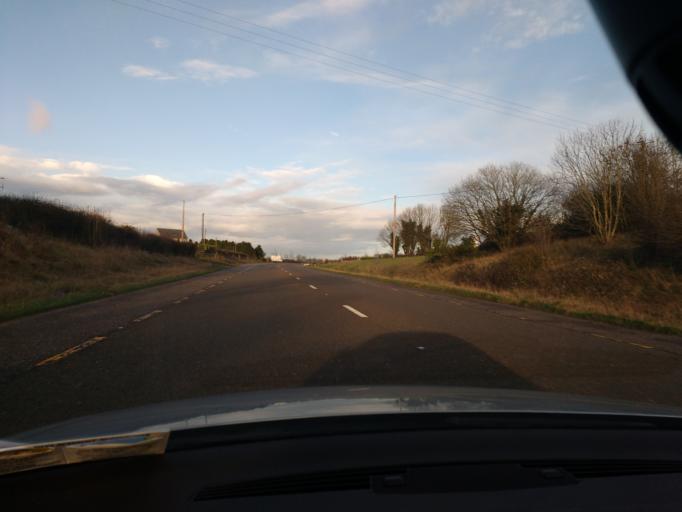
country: IE
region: Munster
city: Thurles
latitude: 52.6821
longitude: -7.6682
